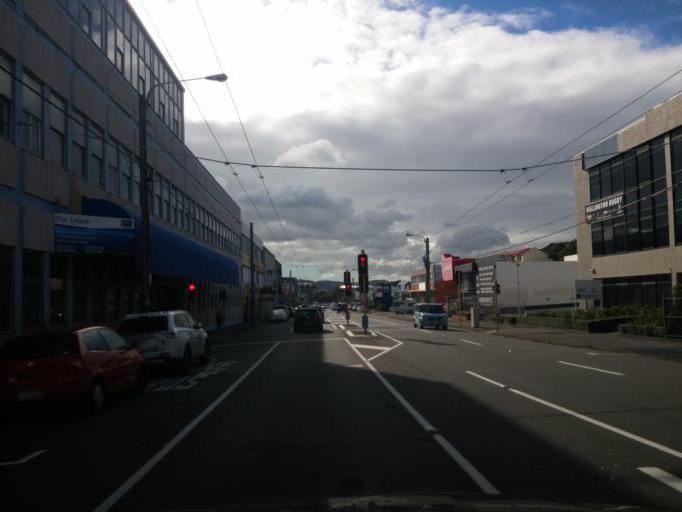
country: NZ
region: Wellington
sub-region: Wellington City
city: Wellington
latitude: -41.3051
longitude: 174.7785
